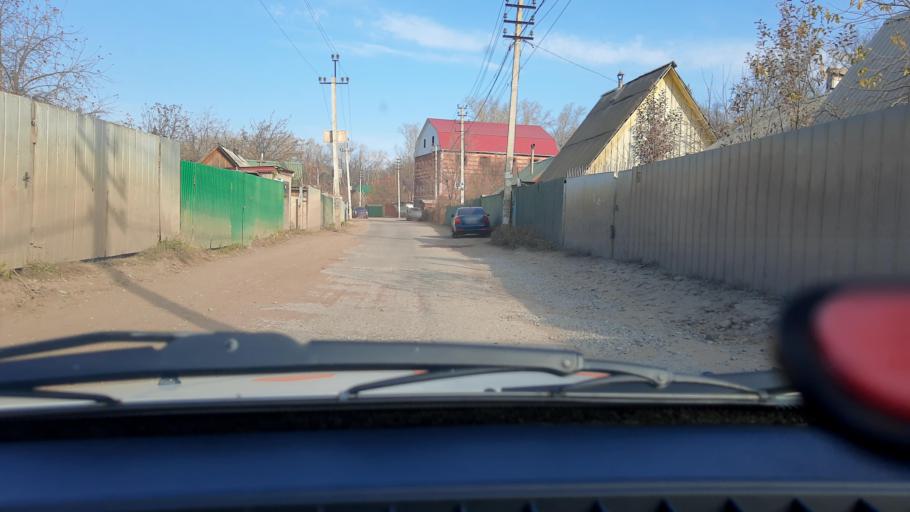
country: RU
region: Bashkortostan
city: Ufa
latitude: 54.6945
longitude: 55.9017
